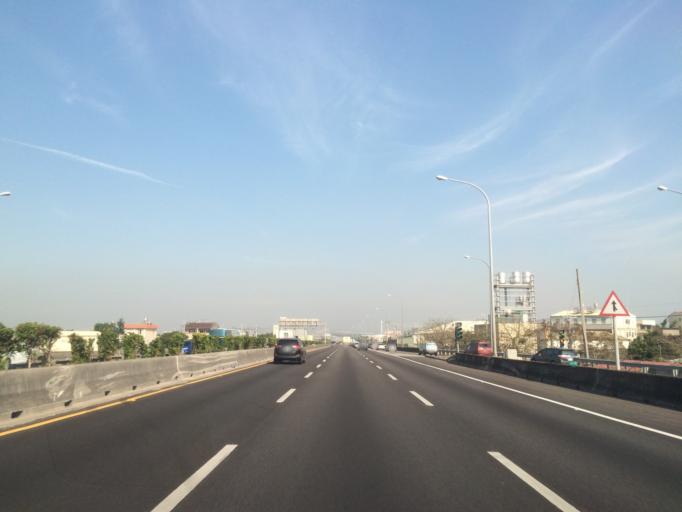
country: TW
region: Taiwan
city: Fengyuan
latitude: 24.2525
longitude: 120.6908
